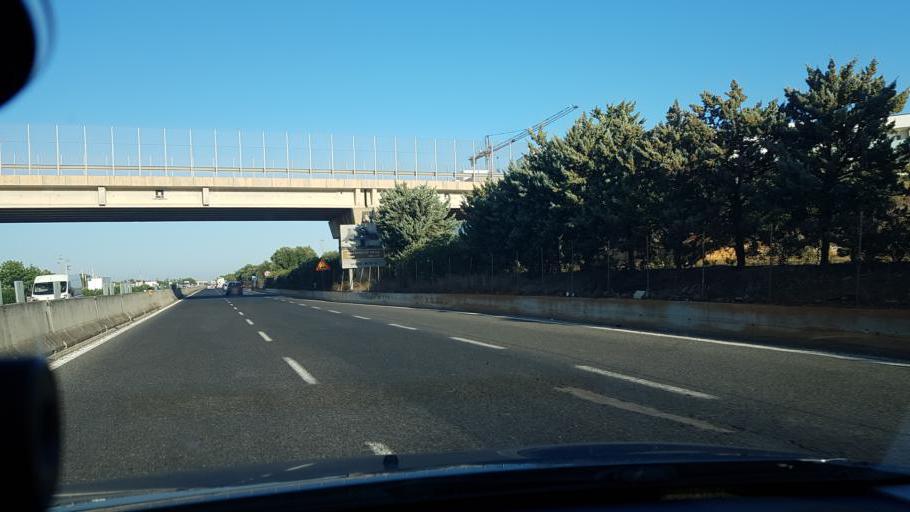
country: IT
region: Apulia
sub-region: Provincia di Bari
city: Monopoli
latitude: 40.9308
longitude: 17.3018
